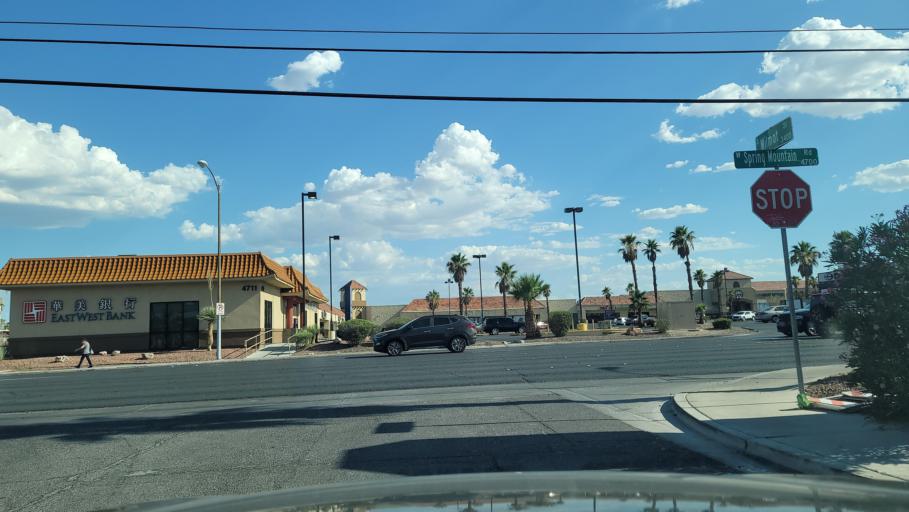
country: US
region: Nevada
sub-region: Clark County
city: Spring Valley
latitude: 36.1265
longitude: -115.2055
